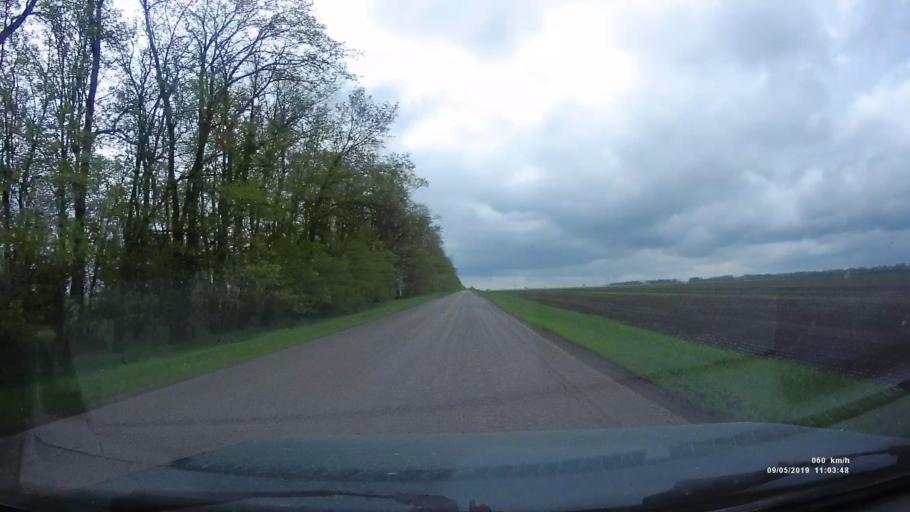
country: RU
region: Krasnodarskiy
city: Kanelovskaya
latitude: 46.8244
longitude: 39.2101
